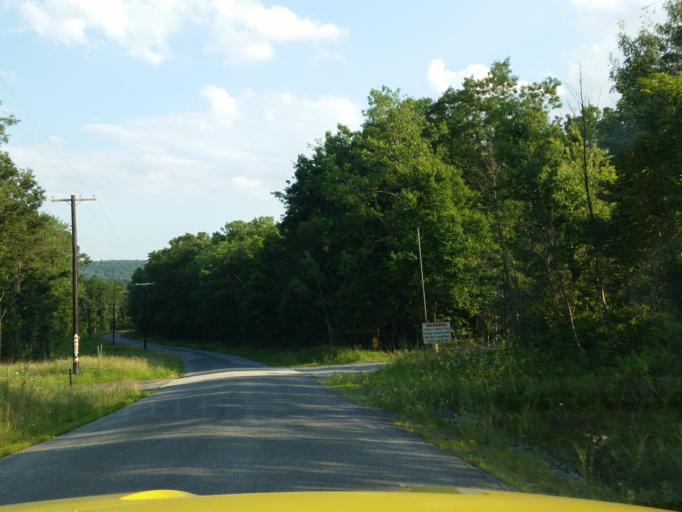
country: US
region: Pennsylvania
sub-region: Dauphin County
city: Williamstown
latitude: 40.4568
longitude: -76.6275
